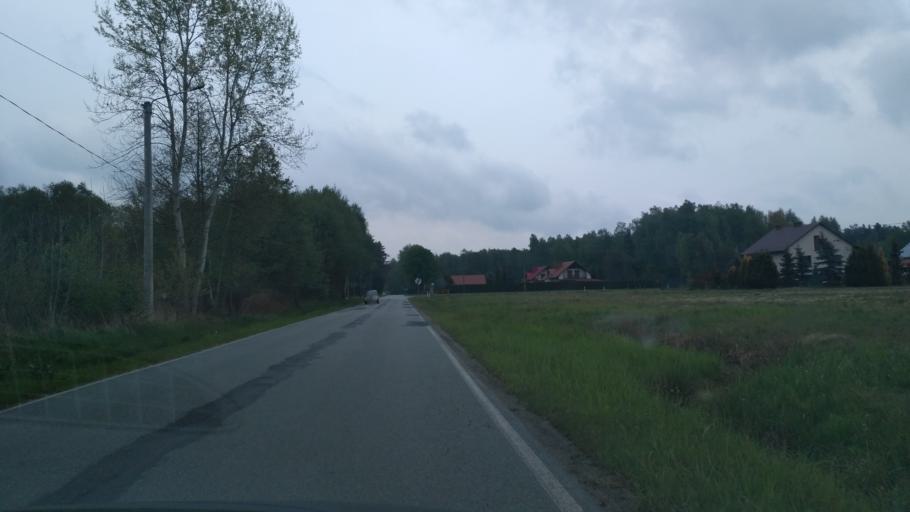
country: PL
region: Subcarpathian Voivodeship
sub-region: Powiat kolbuszowski
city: Kolbuszowa
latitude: 50.1897
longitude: 21.7641
